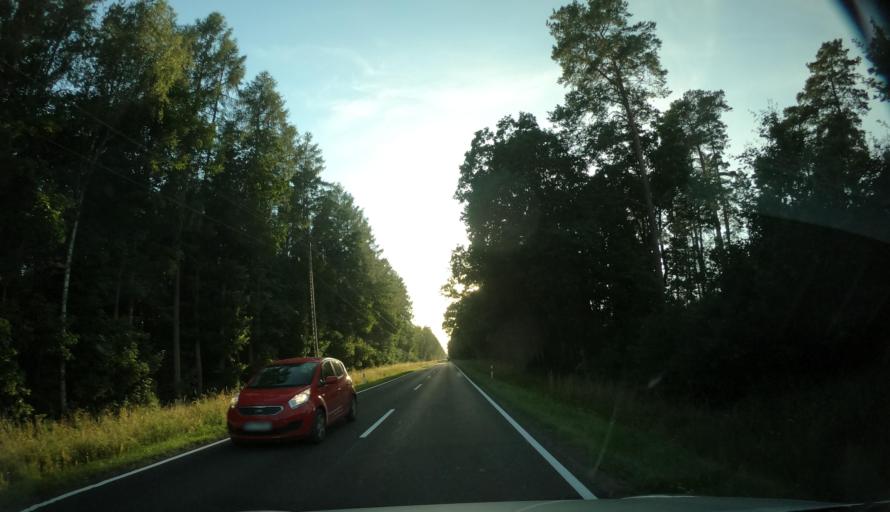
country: PL
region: Kujawsko-Pomorskie
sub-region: Powiat swiecki
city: Swiekatowo
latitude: 53.3074
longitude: 18.0571
